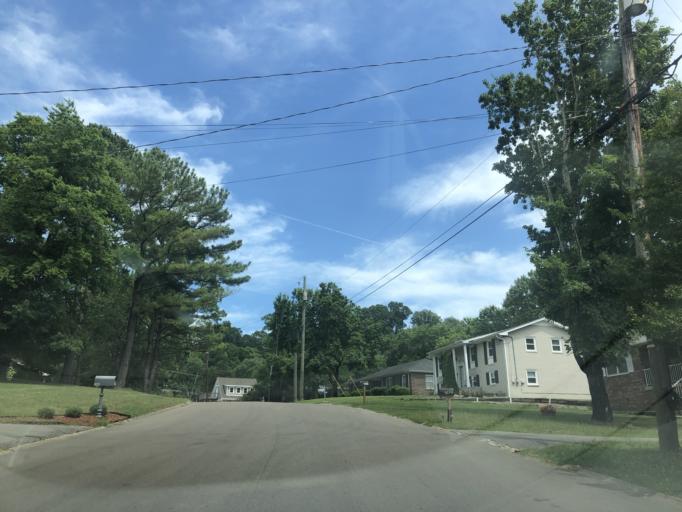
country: US
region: Tennessee
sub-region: Davidson County
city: Belle Meade
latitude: 36.0778
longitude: -86.9372
